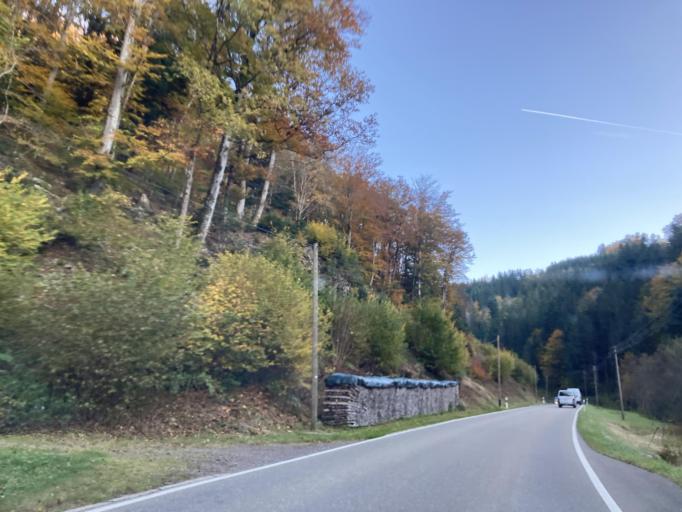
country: DE
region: Baden-Wuerttemberg
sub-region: Freiburg Region
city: Breitnau
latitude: 47.9705
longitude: 8.0719
